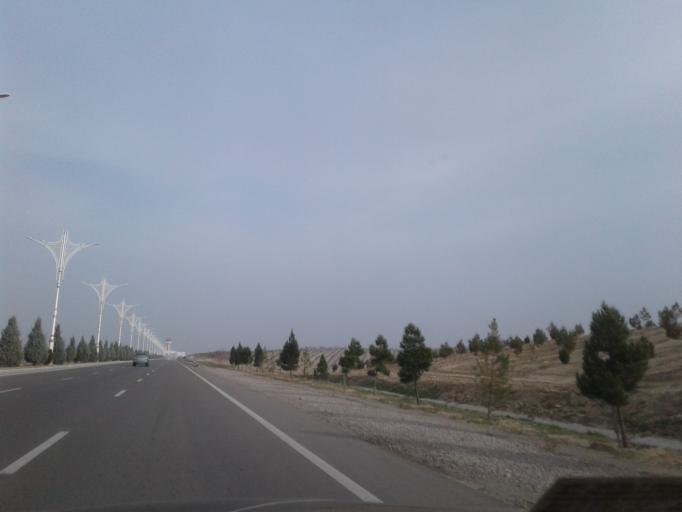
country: TM
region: Ahal
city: Ashgabat
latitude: 37.8783
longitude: 58.4091
